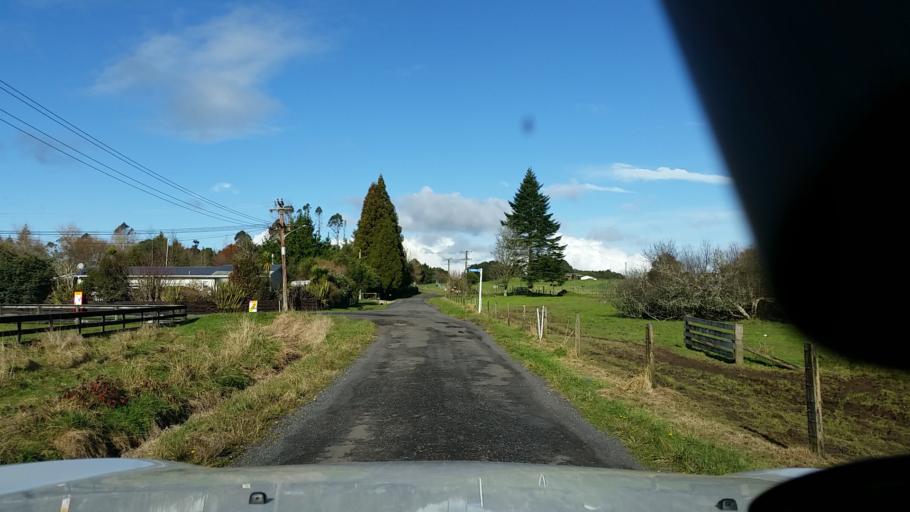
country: NZ
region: Bay of Plenty
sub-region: Rotorua District
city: Rotorua
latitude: -38.0993
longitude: 176.0745
